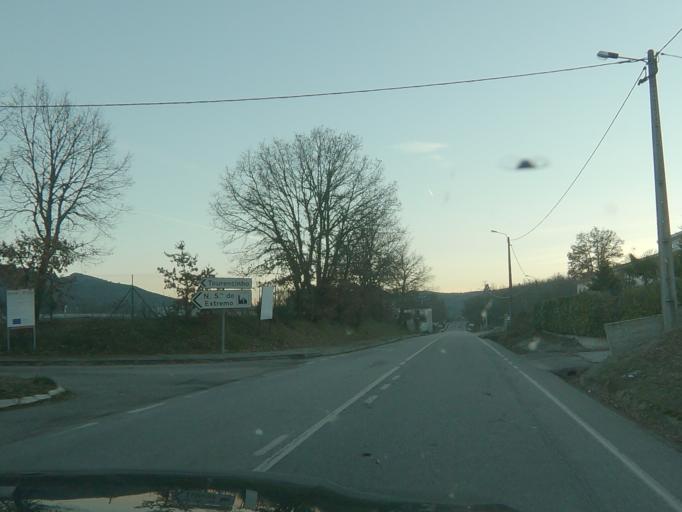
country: PT
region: Vila Real
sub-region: Vila Pouca de Aguiar
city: Vila Pouca de Aguiar
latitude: 41.4311
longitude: -7.6802
